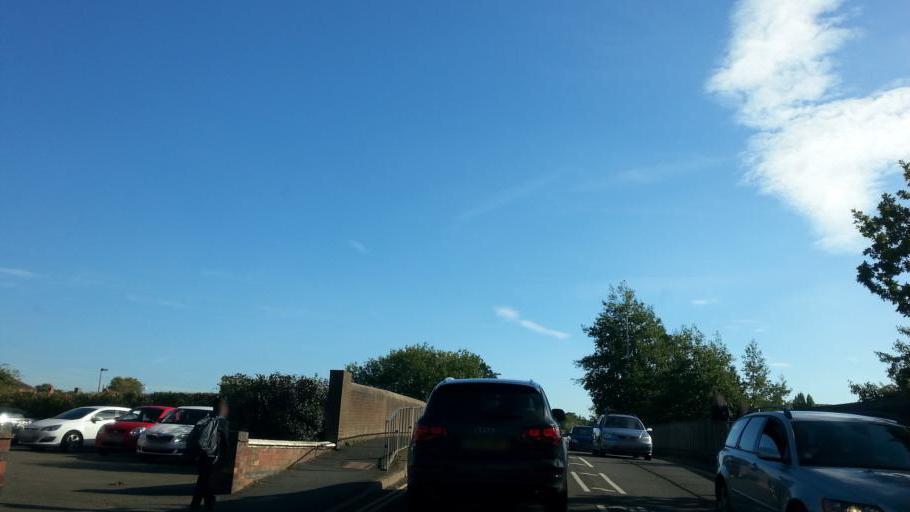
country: GB
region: England
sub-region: Telford and Wrekin
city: Wellington
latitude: 52.7018
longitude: -2.5221
